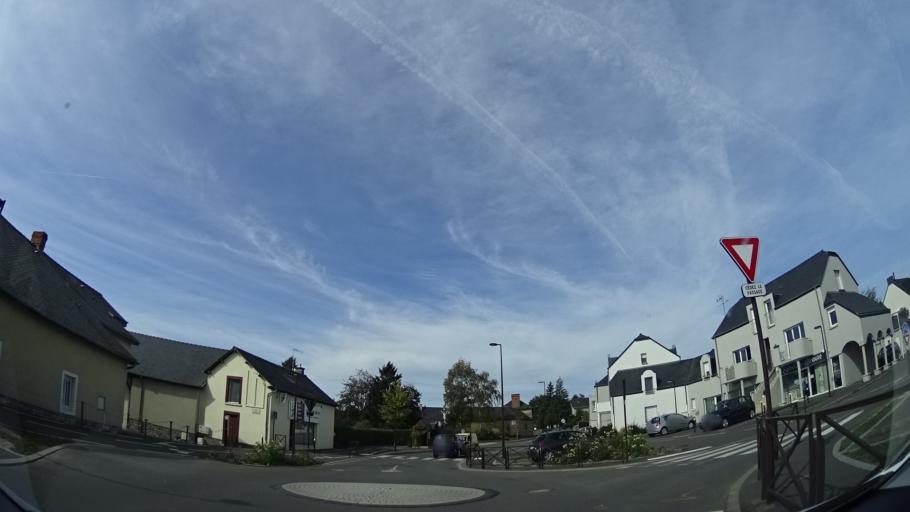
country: FR
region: Brittany
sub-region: Departement d'Ille-et-Vilaine
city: La Meziere
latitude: 48.2184
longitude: -1.7515
